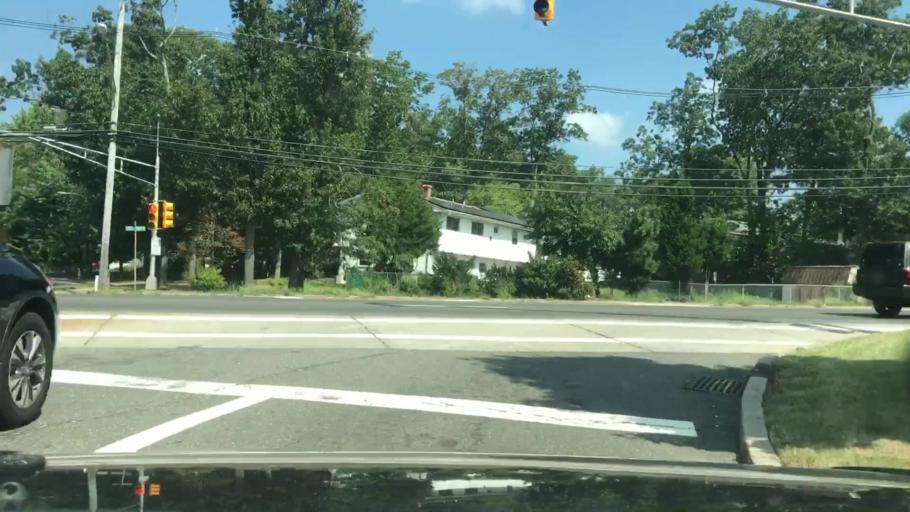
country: US
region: New Jersey
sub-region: Ocean County
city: Silver Ridge
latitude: 39.9924
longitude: -74.2140
